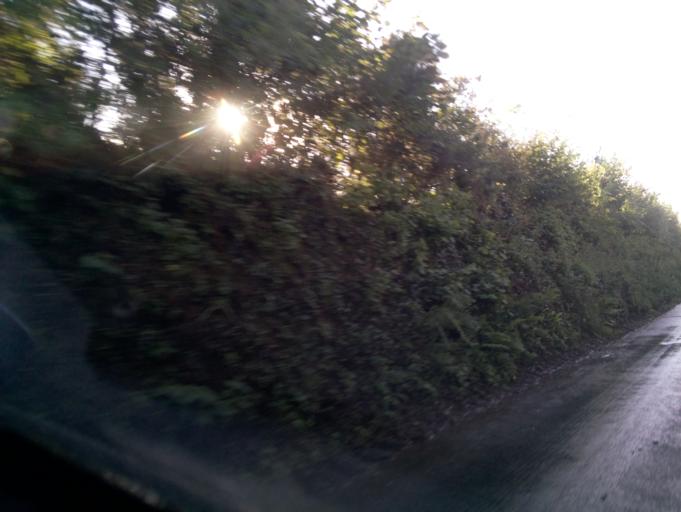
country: GB
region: England
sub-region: Devon
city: Totnes
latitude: 50.3505
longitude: -3.7168
